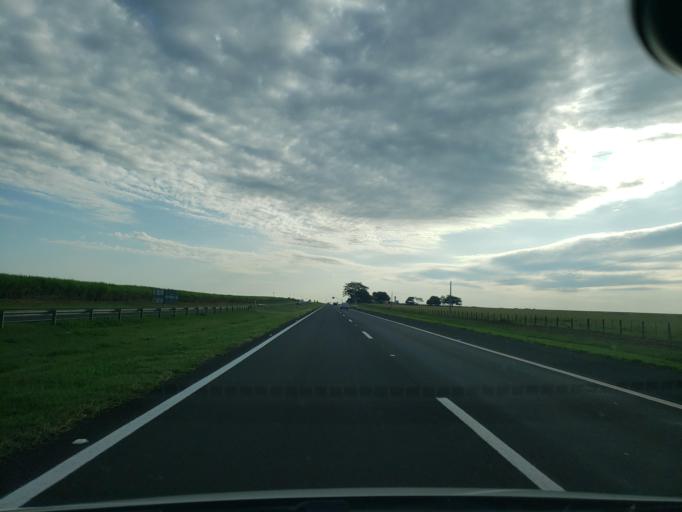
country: BR
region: Sao Paulo
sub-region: Guararapes
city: Guararapes
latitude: -21.2133
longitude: -50.7064
